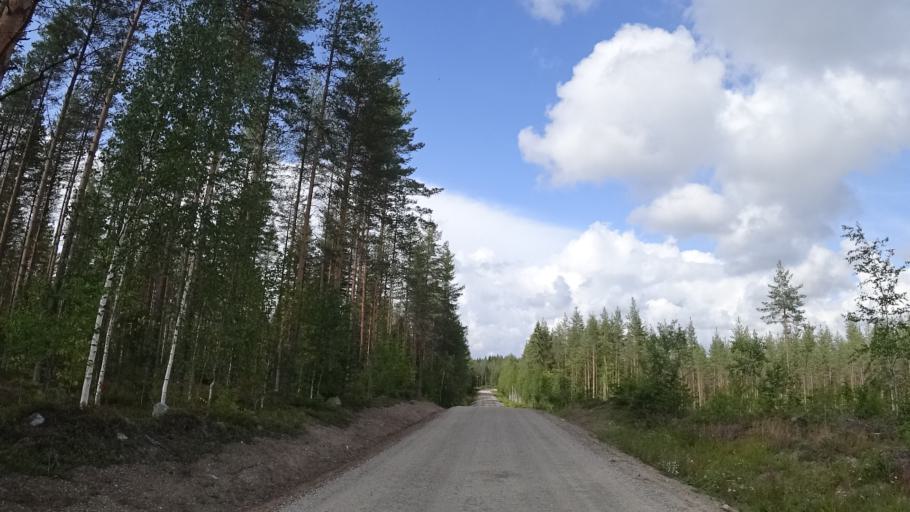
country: FI
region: North Karelia
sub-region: Pielisen Karjala
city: Lieksa
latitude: 63.5884
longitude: 30.1350
